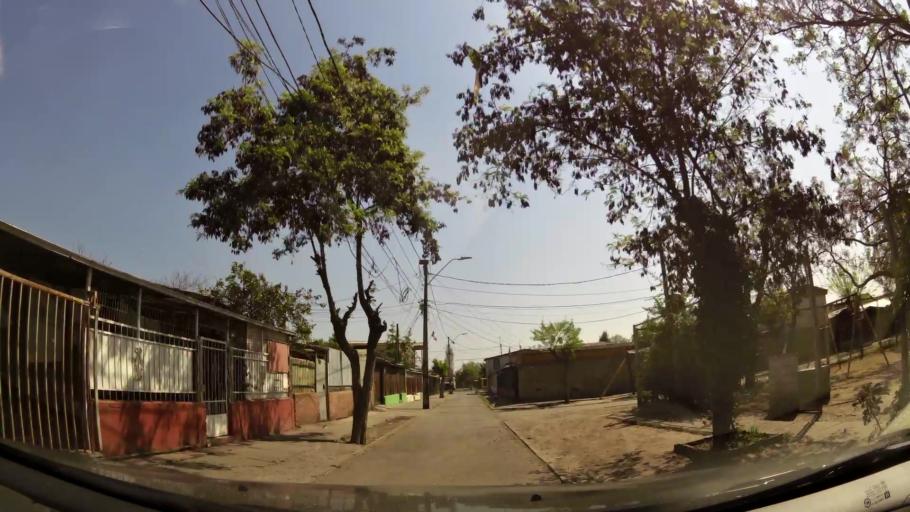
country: CL
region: Santiago Metropolitan
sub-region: Provincia de Maipo
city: San Bernardo
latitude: -33.5778
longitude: -70.7046
